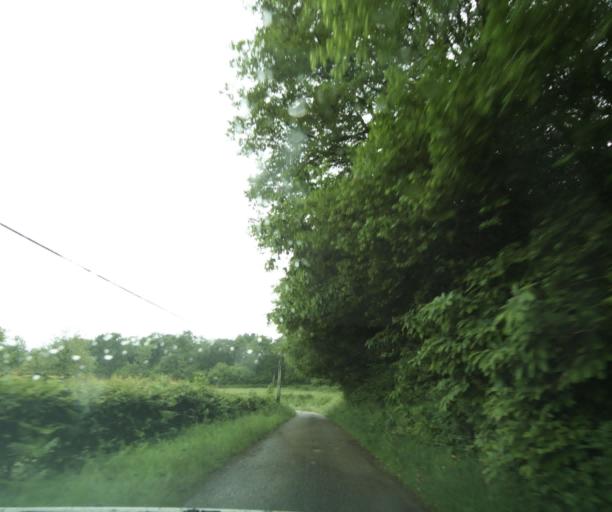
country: FR
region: Bourgogne
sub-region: Departement de Saone-et-Loire
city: Charolles
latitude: 46.5034
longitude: 4.2958
